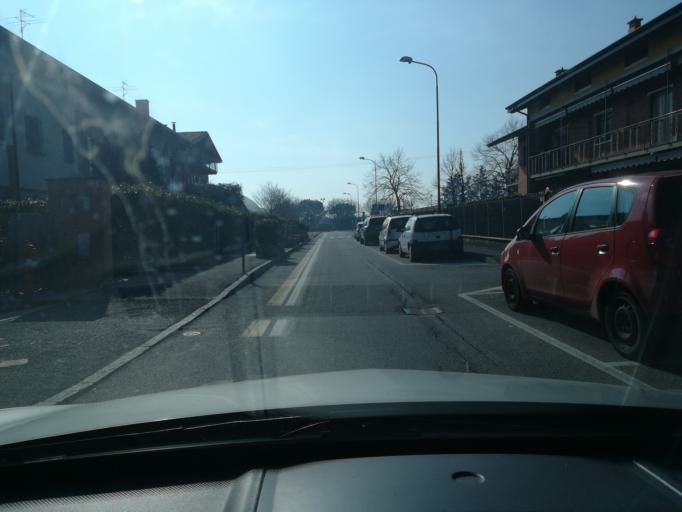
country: IT
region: Lombardy
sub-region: Provincia di Bergamo
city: Stezzano
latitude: 45.6464
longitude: 9.6486
